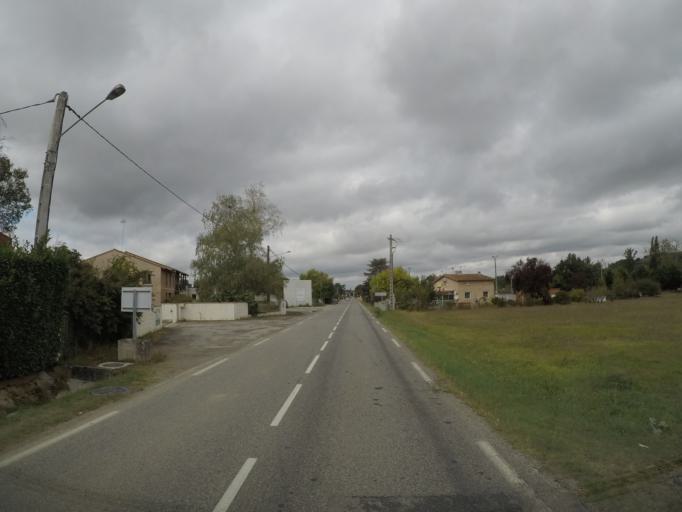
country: FR
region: Midi-Pyrenees
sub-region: Departement de la Haute-Garonne
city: Gaillac-Toulza
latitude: 43.1688
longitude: 1.4133
